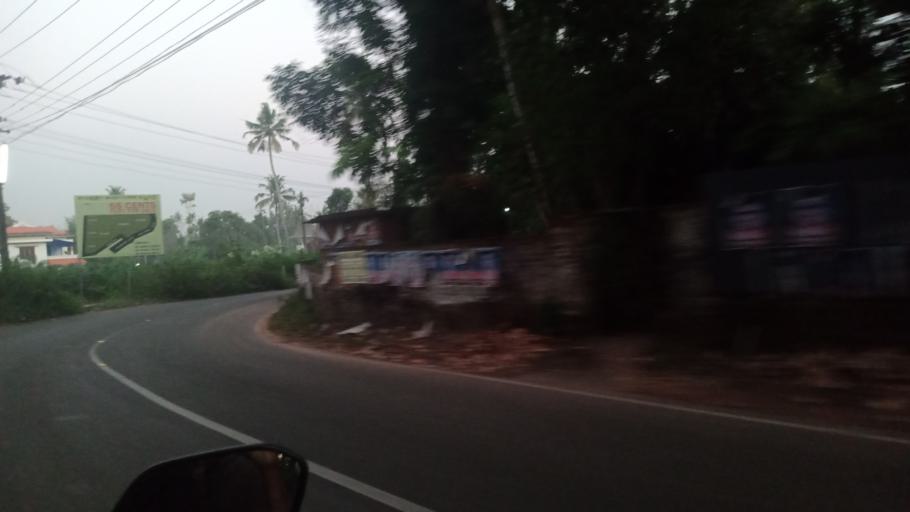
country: IN
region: Kerala
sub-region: Ernakulam
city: Angamali
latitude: 10.2003
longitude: 76.3052
